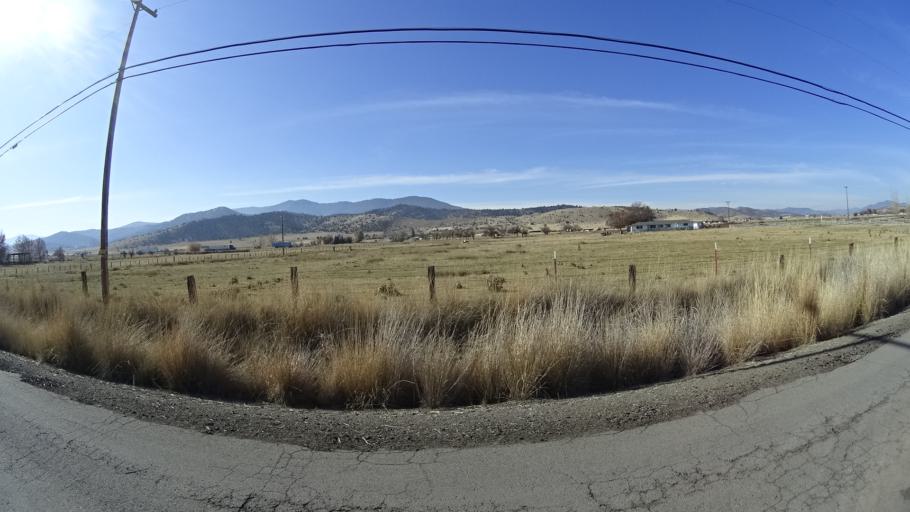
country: US
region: California
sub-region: Siskiyou County
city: Montague
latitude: 41.6341
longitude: -122.5218
